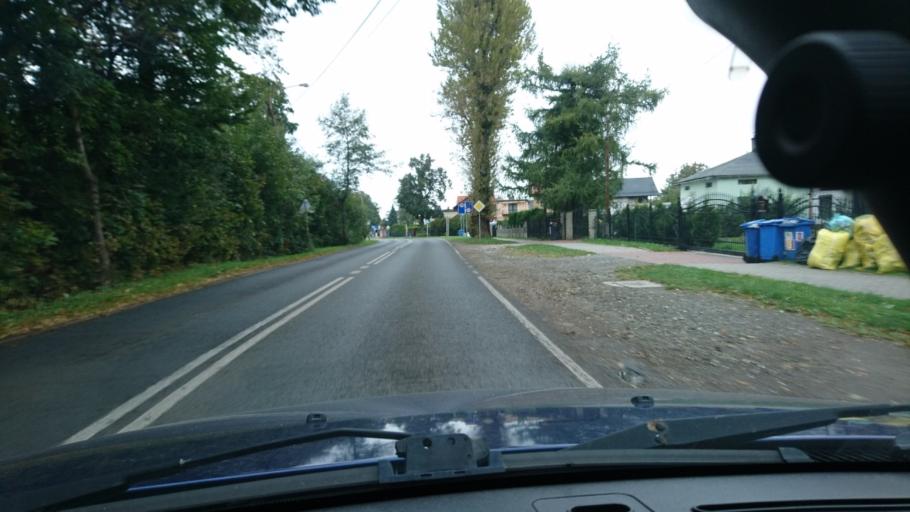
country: PL
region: Silesian Voivodeship
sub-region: Powiat bielski
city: Jaworze
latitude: 49.8004
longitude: 18.9840
